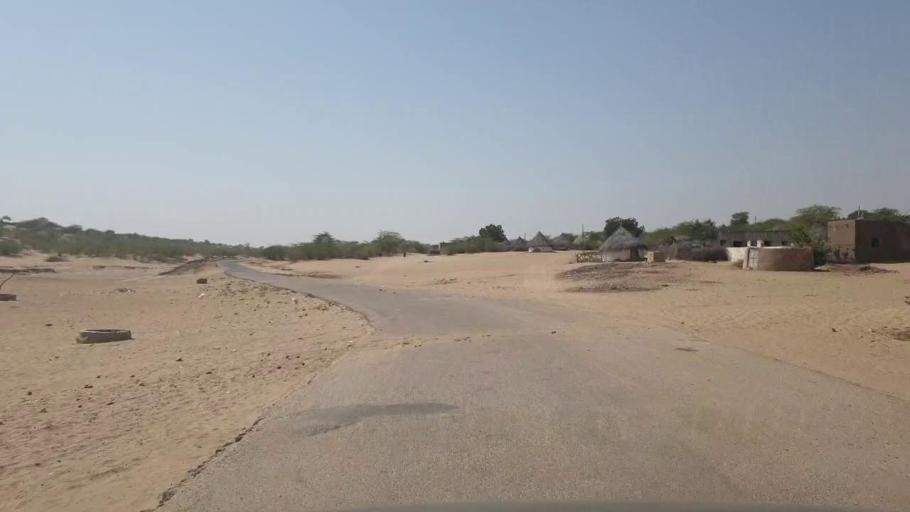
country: PK
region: Sindh
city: Chor
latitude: 25.5717
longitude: 70.1818
